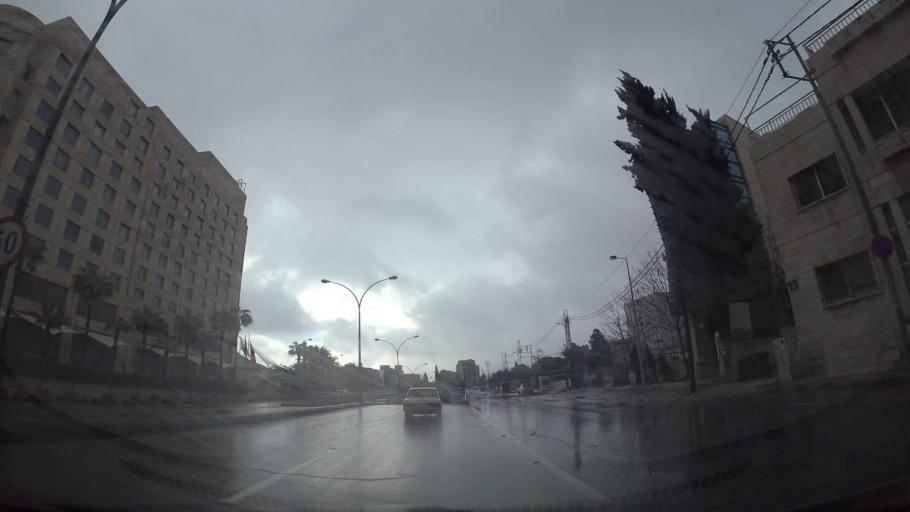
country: JO
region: Amman
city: Amman
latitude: 31.9559
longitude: 35.9086
